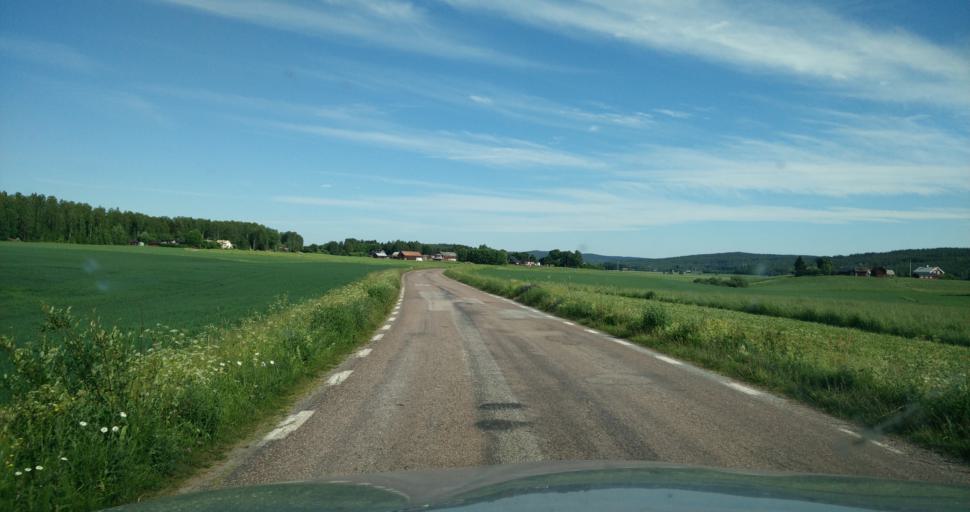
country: SE
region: Dalarna
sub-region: Hedemora Kommun
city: Langshyttan
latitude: 60.3884
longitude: 15.9720
